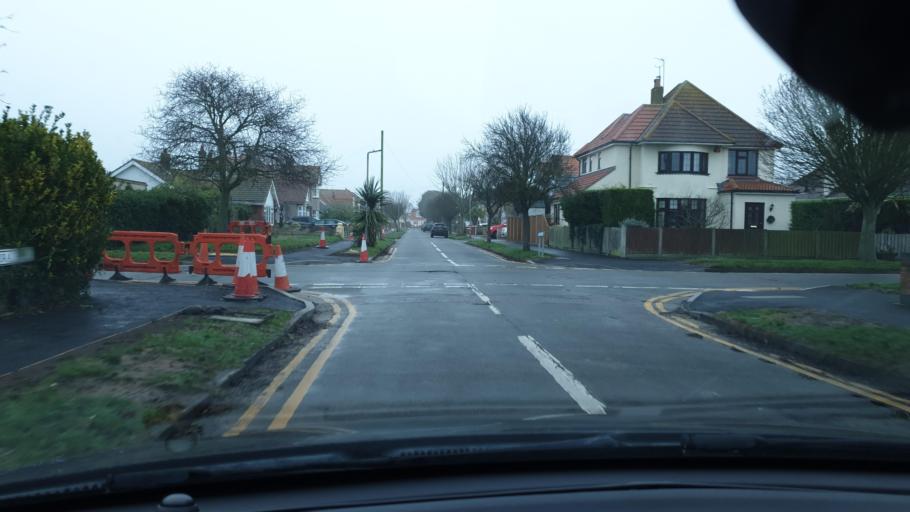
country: GB
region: England
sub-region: Essex
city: Clacton-on-Sea
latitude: 51.8002
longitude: 1.1878
